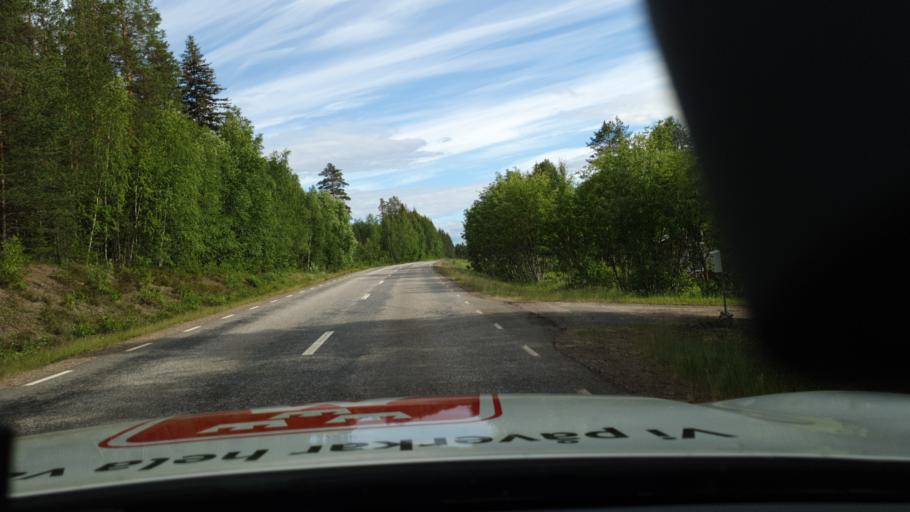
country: SE
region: Norrbotten
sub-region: Overkalix Kommun
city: OEverkalix
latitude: 66.4952
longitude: 22.7743
